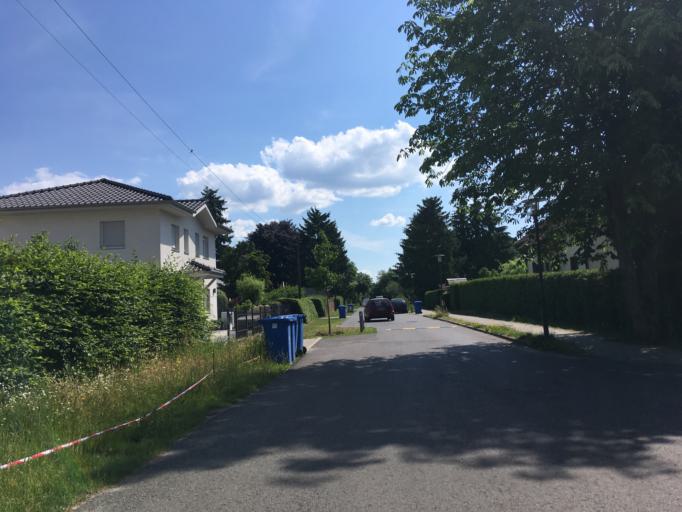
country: DE
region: Berlin
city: Hellersdorf
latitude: 52.5359
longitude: 13.6371
